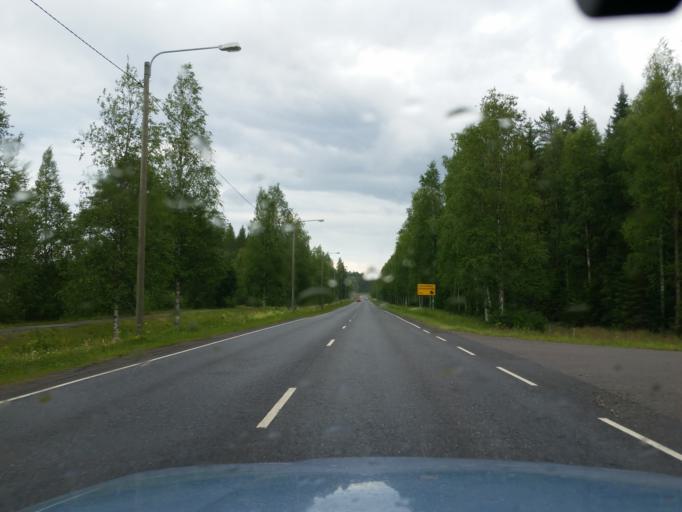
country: FI
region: Southern Savonia
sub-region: Pieksaemaeki
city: Juva
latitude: 61.8987
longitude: 27.8157
